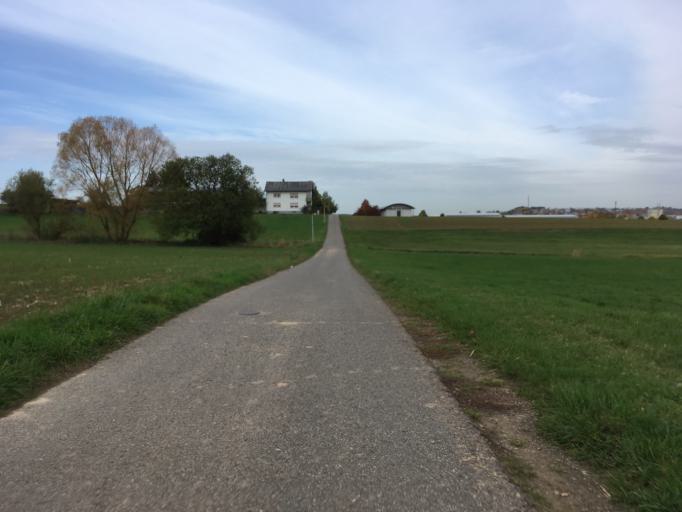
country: DE
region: Baden-Wuerttemberg
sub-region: Karlsruhe Region
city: Buchen
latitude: 49.5123
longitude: 9.3241
